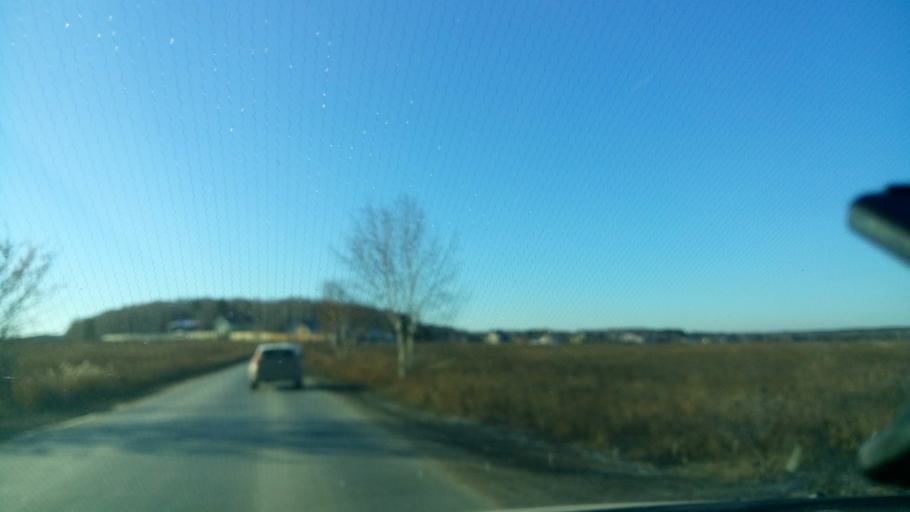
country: RU
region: Sverdlovsk
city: Gornyy Shchit
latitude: 56.7218
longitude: 60.5244
